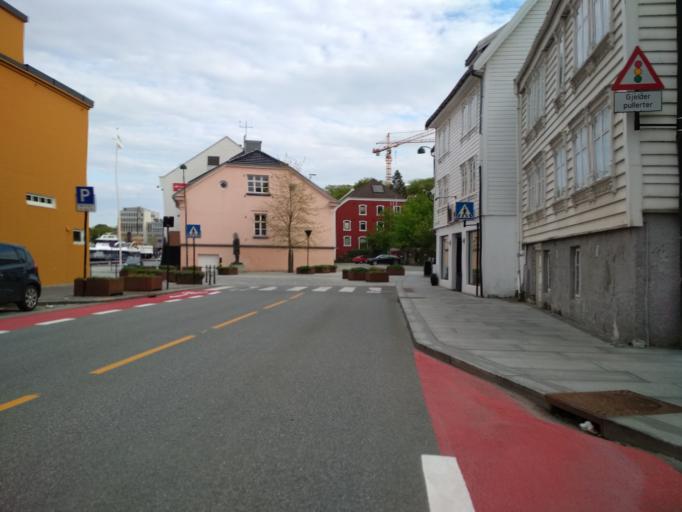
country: NO
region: Rogaland
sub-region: Stavanger
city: Stavanger
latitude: 58.9725
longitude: 5.7263
